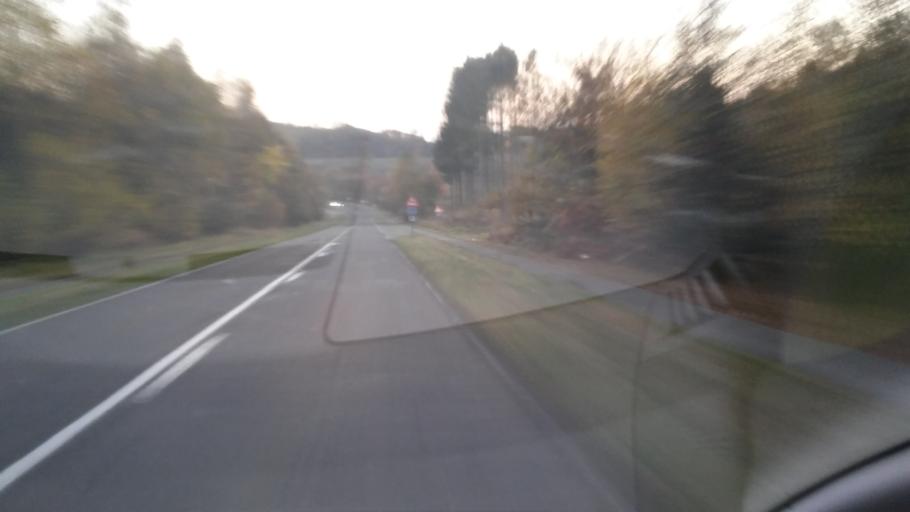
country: BE
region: Wallonia
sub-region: Province du Luxembourg
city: Etalle
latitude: 49.6442
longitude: 5.5718
